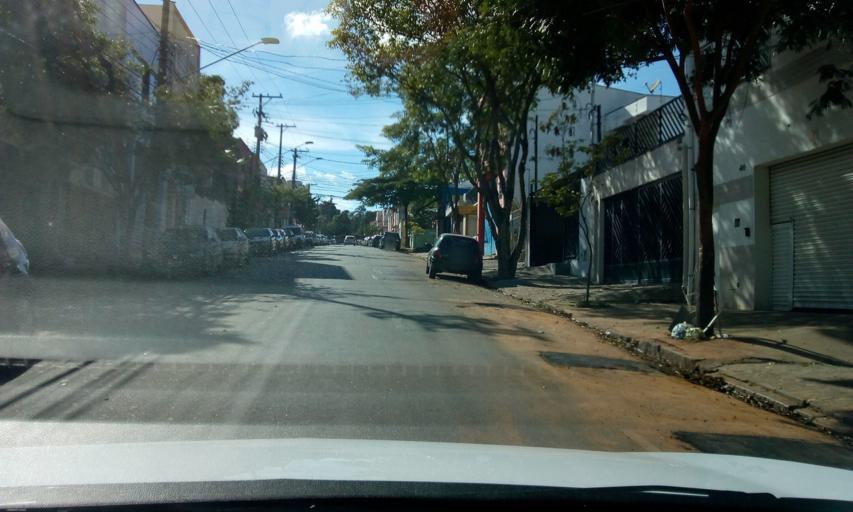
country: BR
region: Sao Paulo
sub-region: Sao Paulo
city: Sao Paulo
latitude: -23.5640
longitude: -46.6001
